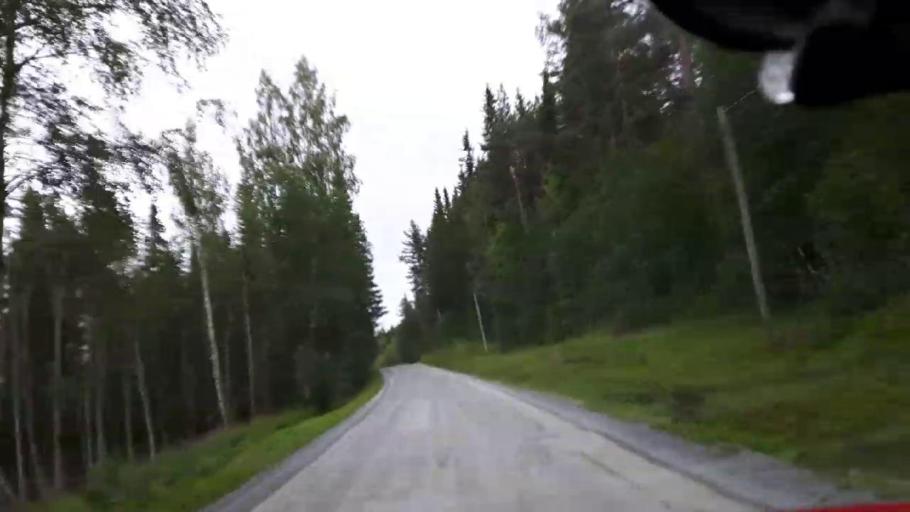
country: SE
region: Jaemtland
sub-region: Braecke Kommun
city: Braecke
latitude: 63.0864
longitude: 15.2644
